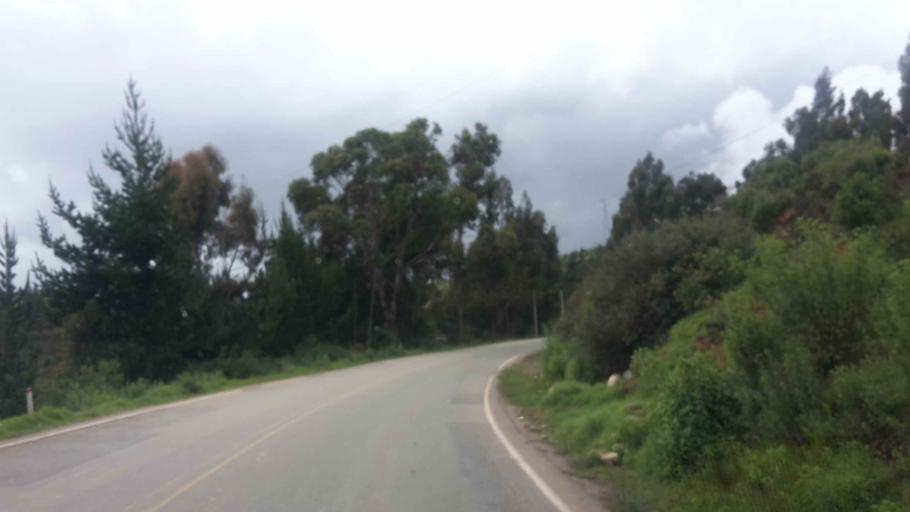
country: BO
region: Cochabamba
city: Totora
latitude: -17.5707
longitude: -65.3323
